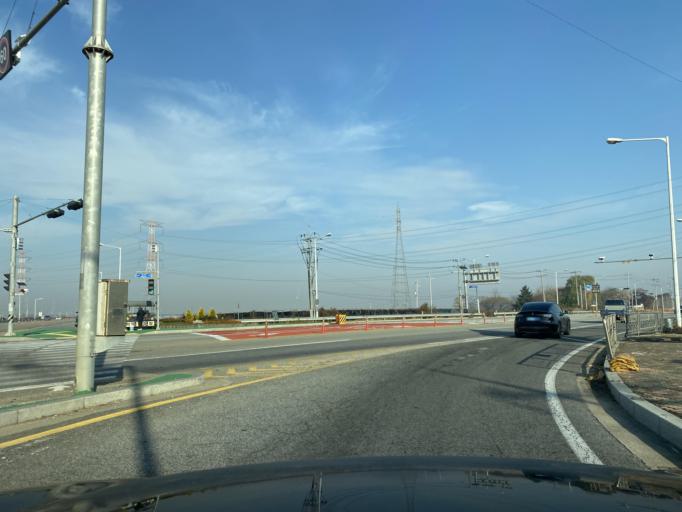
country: KR
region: Chungcheongnam-do
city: Yesan
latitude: 36.7390
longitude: 126.8589
